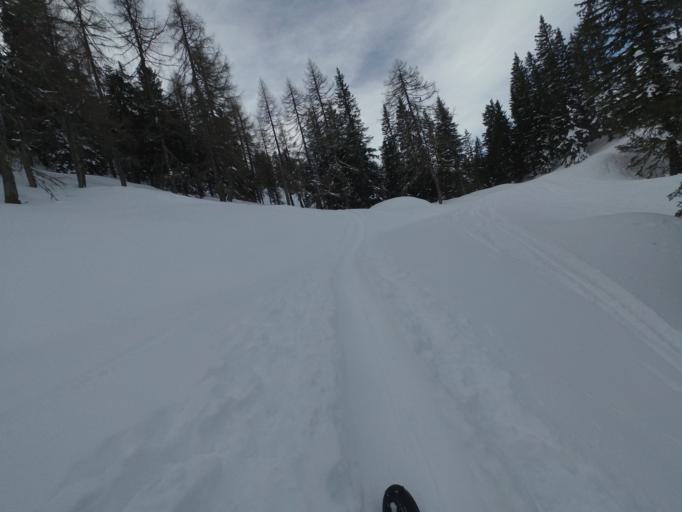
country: AT
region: Salzburg
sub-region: Politischer Bezirk Zell am See
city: Lend
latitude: 47.2693
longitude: 13.0190
